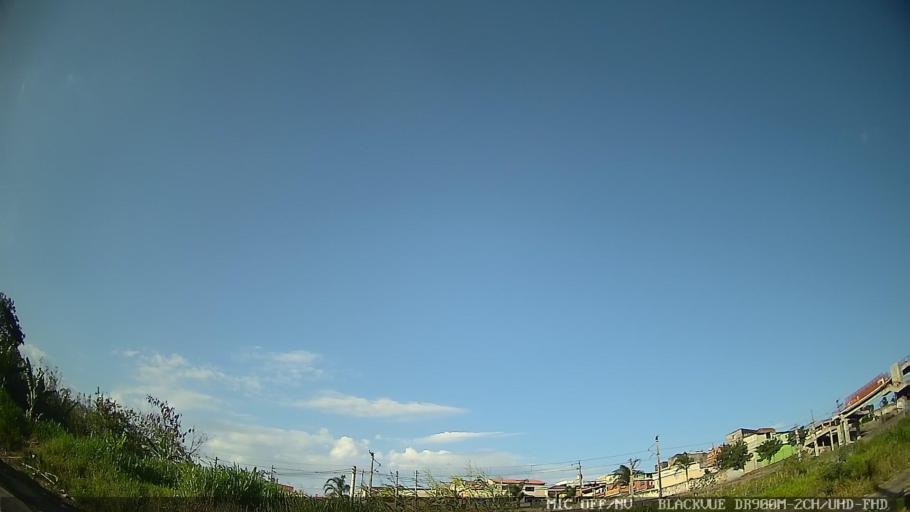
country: BR
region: Sao Paulo
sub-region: Ferraz De Vasconcelos
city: Ferraz de Vasconcelos
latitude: -23.5548
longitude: -46.3922
